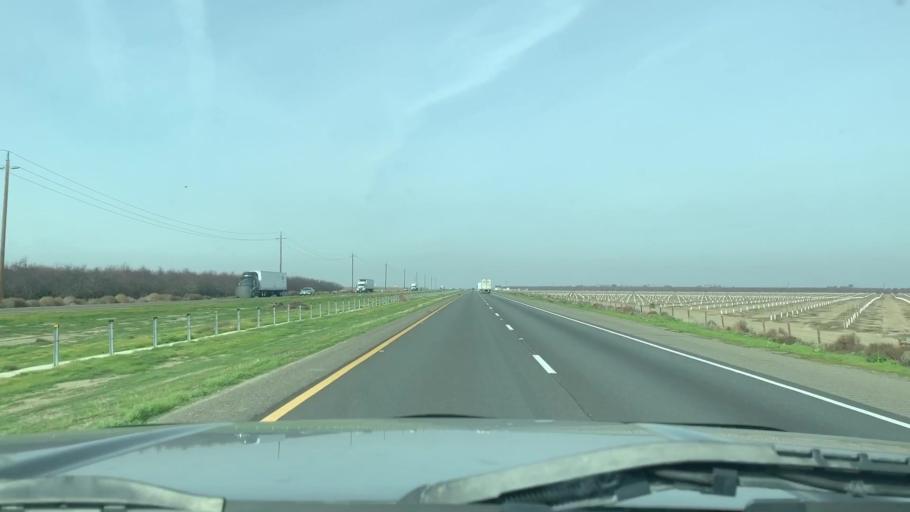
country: US
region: California
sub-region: Fresno County
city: Huron
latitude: 36.2323
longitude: -120.2299
